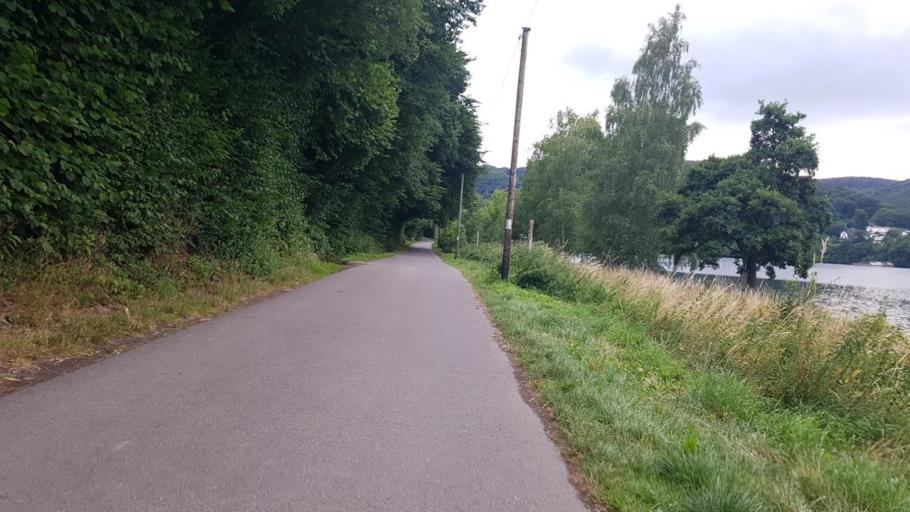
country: DE
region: North Rhine-Westphalia
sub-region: Regierungsbezirk Koln
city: Nideggen
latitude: 50.7133
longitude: 6.4463
